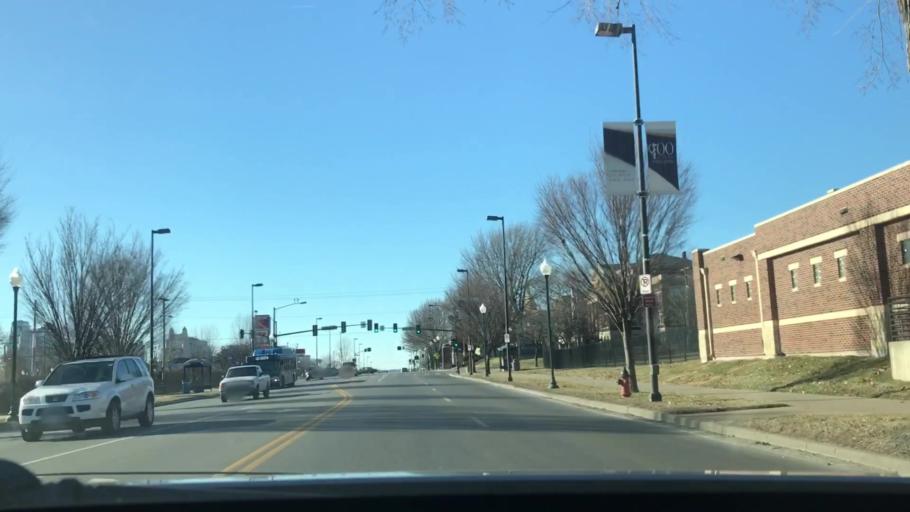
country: US
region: Missouri
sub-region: Jackson County
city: Kansas City
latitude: 39.1066
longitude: -94.5589
